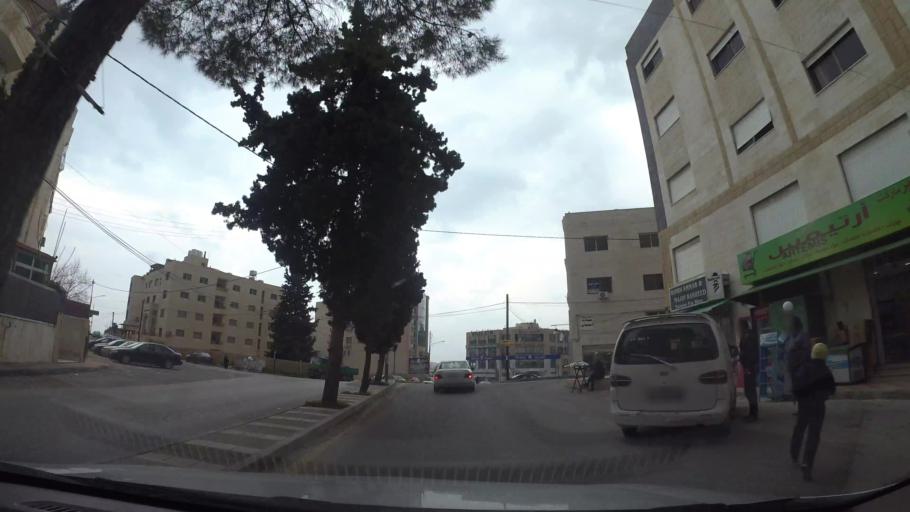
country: JO
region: Amman
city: Umm as Summaq
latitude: 31.8876
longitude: 35.8512
